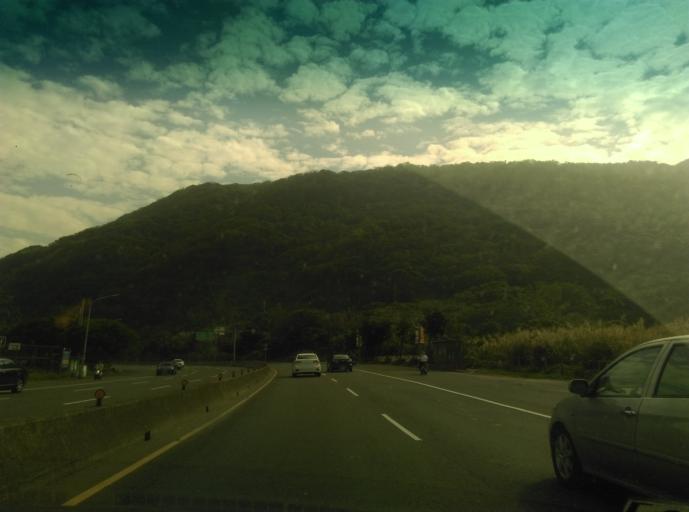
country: TW
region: Taiwan
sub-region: Keelung
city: Keelung
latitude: 25.1867
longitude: 121.6833
